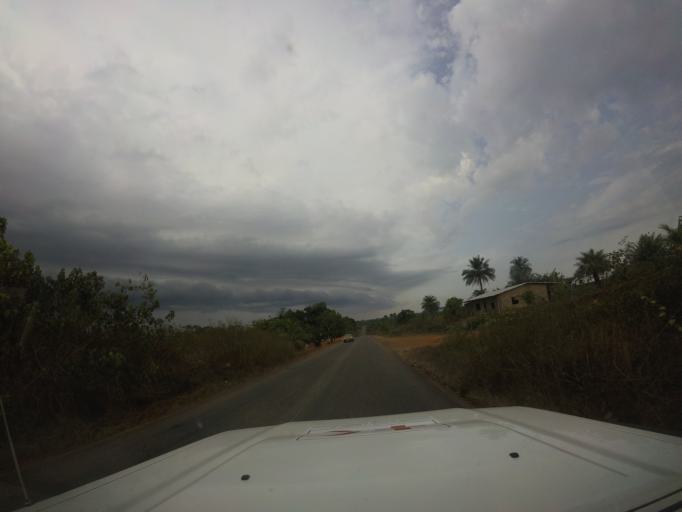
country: LR
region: Bomi
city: Tubmanburg
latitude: 6.7089
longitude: -10.9304
